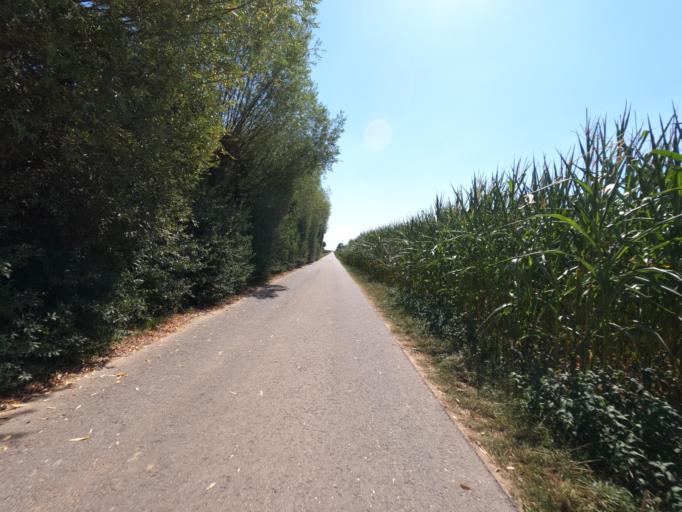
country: DE
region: North Rhine-Westphalia
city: Huckelhoven
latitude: 51.0969
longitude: 6.2540
